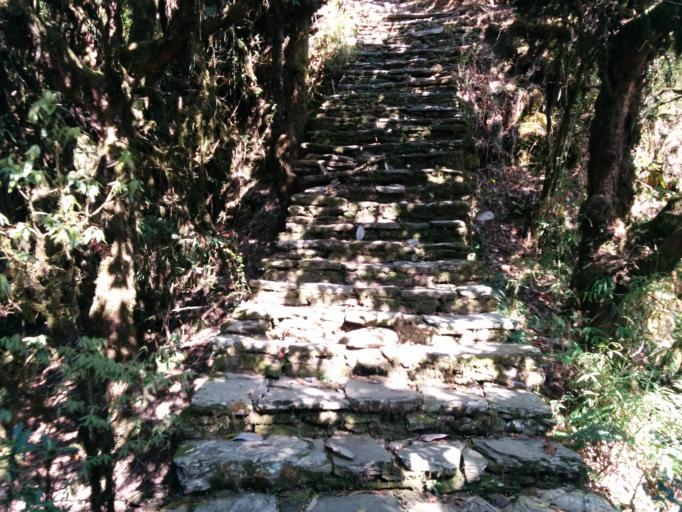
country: NP
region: Western Region
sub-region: Gandaki Zone
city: Pokhara
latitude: 28.2294
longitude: 83.7964
